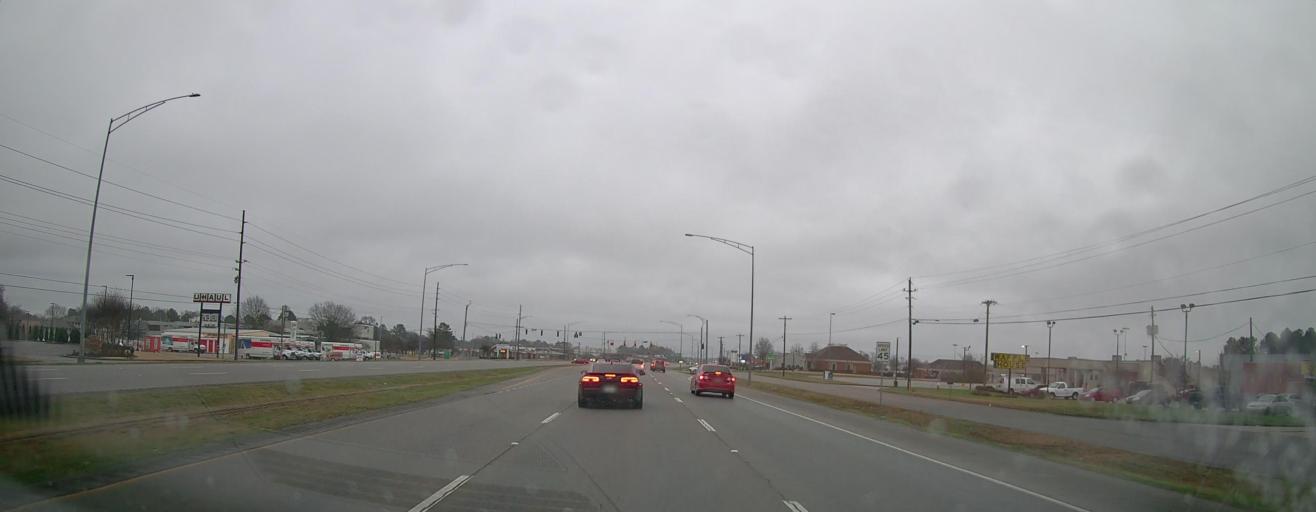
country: US
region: Alabama
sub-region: Morgan County
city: Decatur
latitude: 34.5781
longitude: -87.0190
